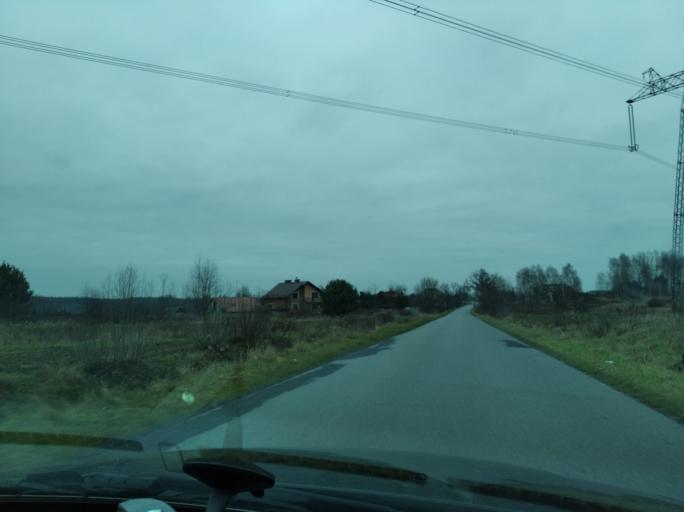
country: PL
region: Subcarpathian Voivodeship
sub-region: Powiat lancucki
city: Rakszawa
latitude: 50.1852
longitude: 22.2521
